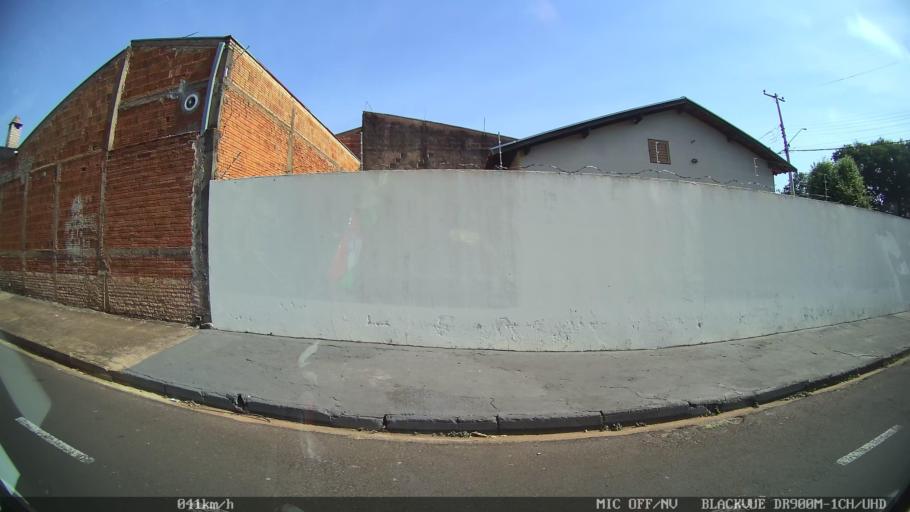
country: BR
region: Sao Paulo
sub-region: Sao Jose Do Rio Preto
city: Sao Jose do Rio Preto
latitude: -20.7883
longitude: -49.4290
